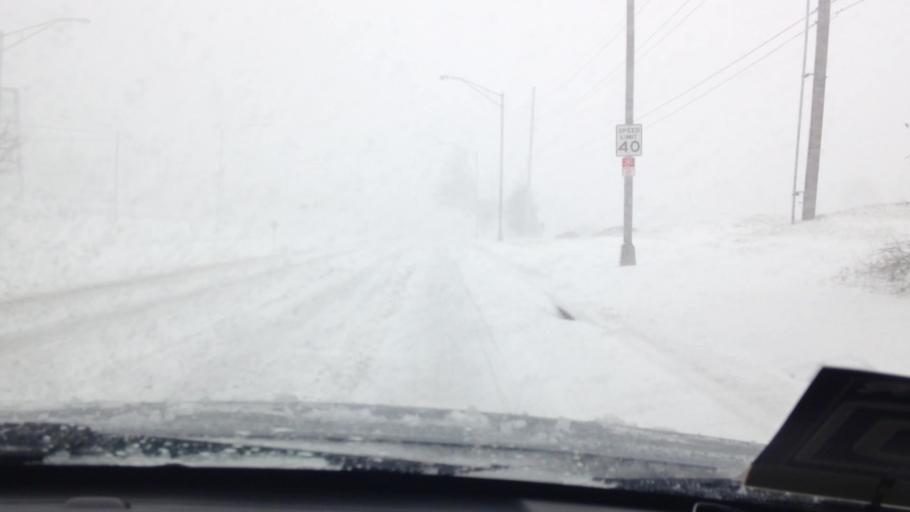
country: US
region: Kansas
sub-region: Johnson County
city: Shawnee
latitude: 39.1167
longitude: -94.7336
